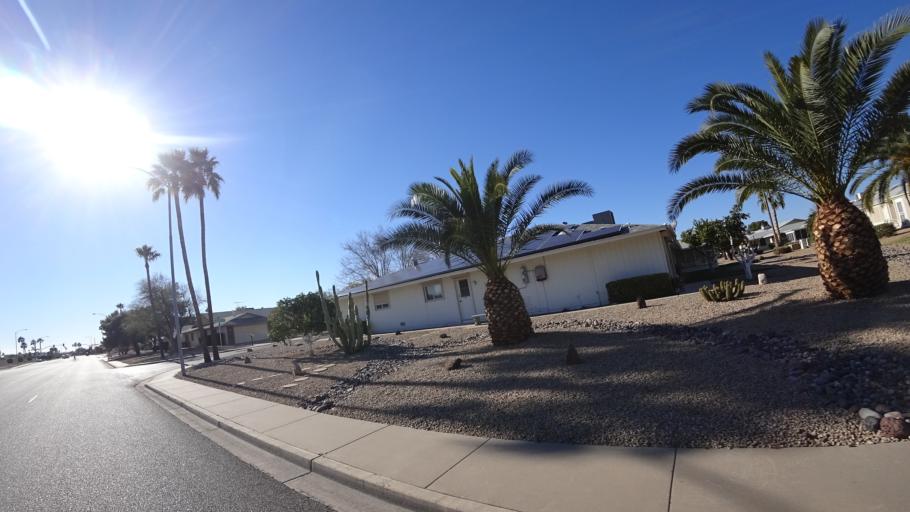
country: US
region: Arizona
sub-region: Maricopa County
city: Sun City West
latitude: 33.6512
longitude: -112.3358
